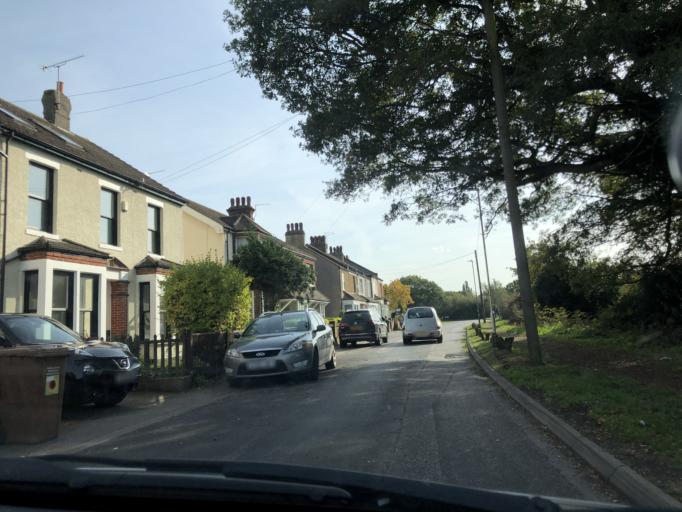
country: GB
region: England
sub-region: Kent
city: Dartford
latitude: 51.4376
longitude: 0.1945
